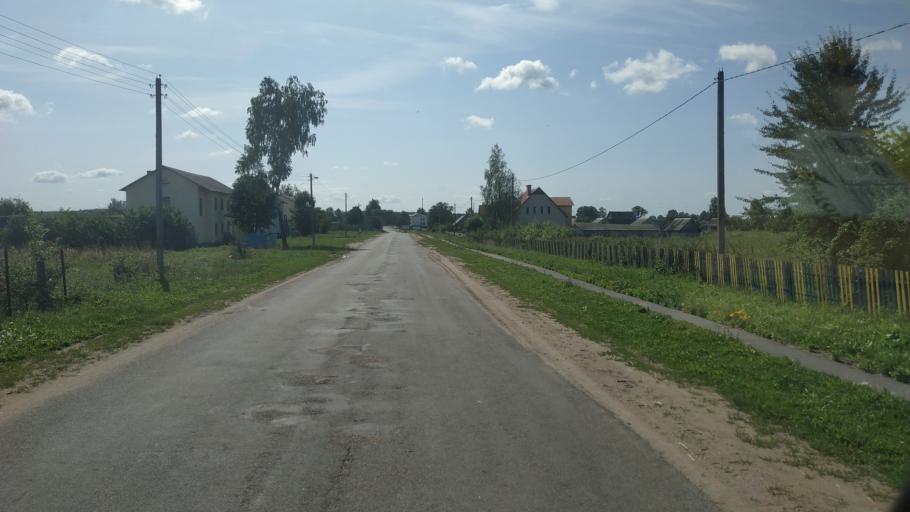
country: BY
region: Mogilev
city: Poselok Voskhod
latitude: 53.7077
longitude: 30.5013
